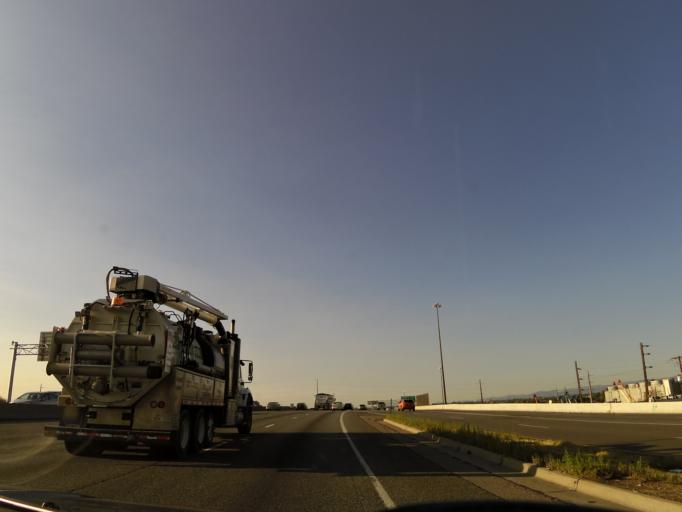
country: US
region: Colorado
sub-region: Denver County
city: Denver
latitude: 39.7386
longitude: -105.0140
